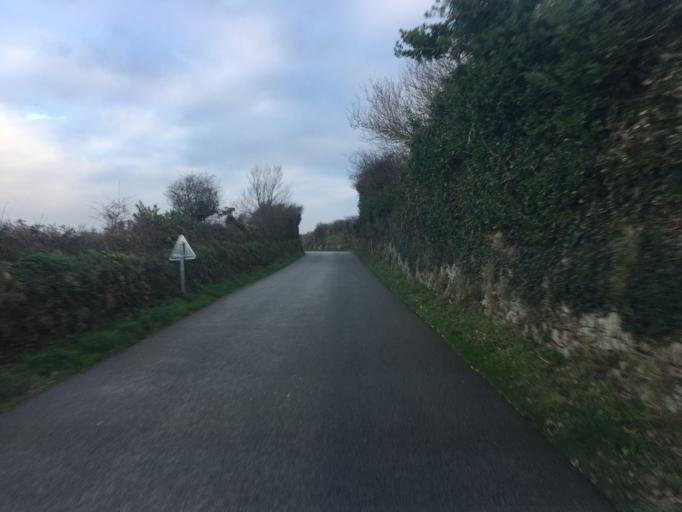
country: FR
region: Lower Normandy
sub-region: Departement de la Manche
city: Beaumont-Hague
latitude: 49.7118
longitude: -1.9280
